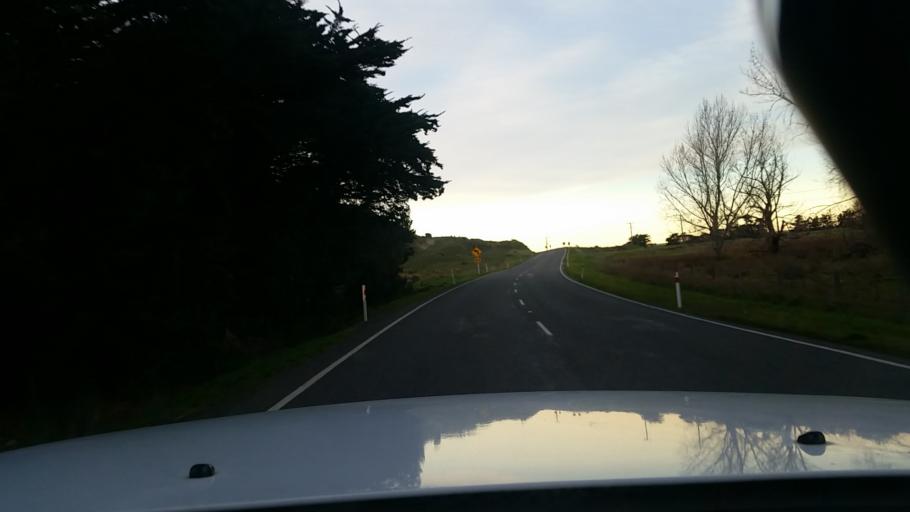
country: NZ
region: Canterbury
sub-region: Selwyn District
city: Lincoln
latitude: -43.7470
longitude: 172.6122
